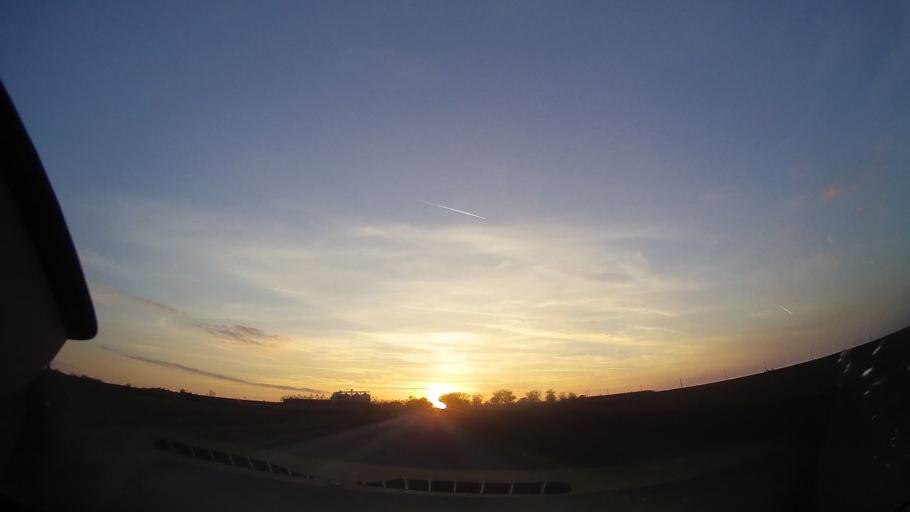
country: RO
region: Constanta
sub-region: Comuna Mereni
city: Mereni
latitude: 44.0225
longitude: 28.3556
